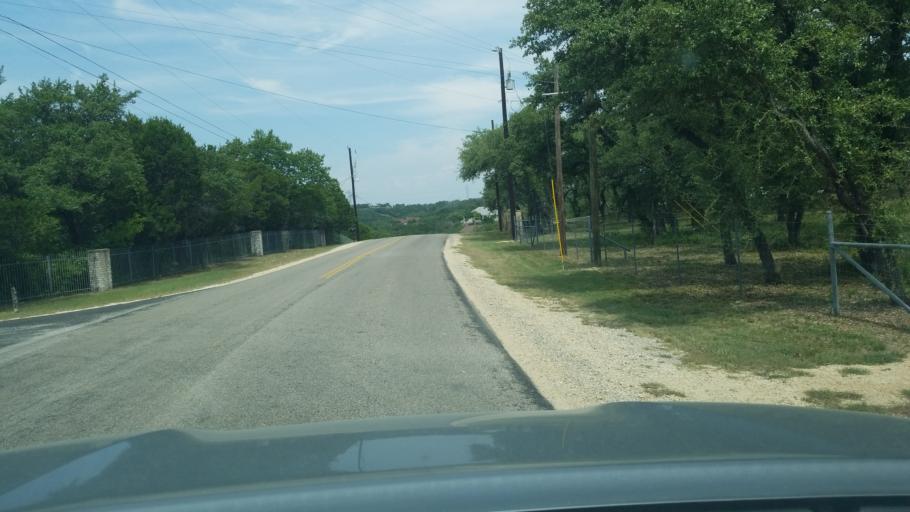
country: US
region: Texas
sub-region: Comal County
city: Bulverde
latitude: 29.7747
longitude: -98.4297
